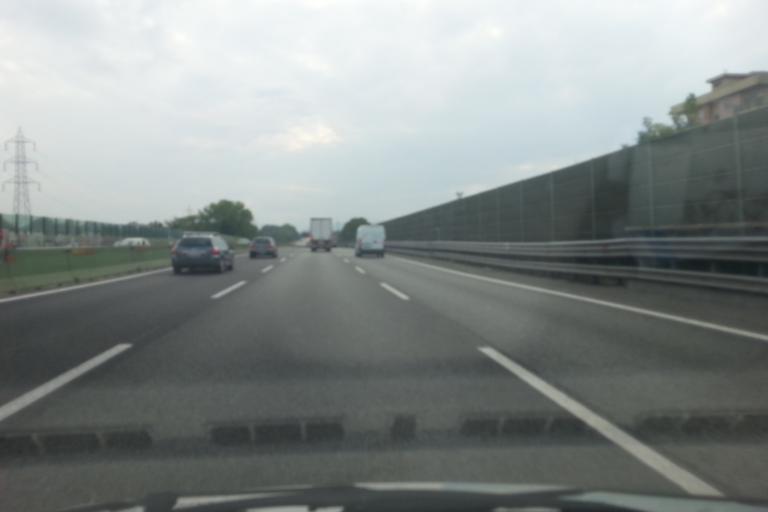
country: IT
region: Piedmont
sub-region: Provincia di Torino
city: Collegno
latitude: 45.0926
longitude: 7.5675
